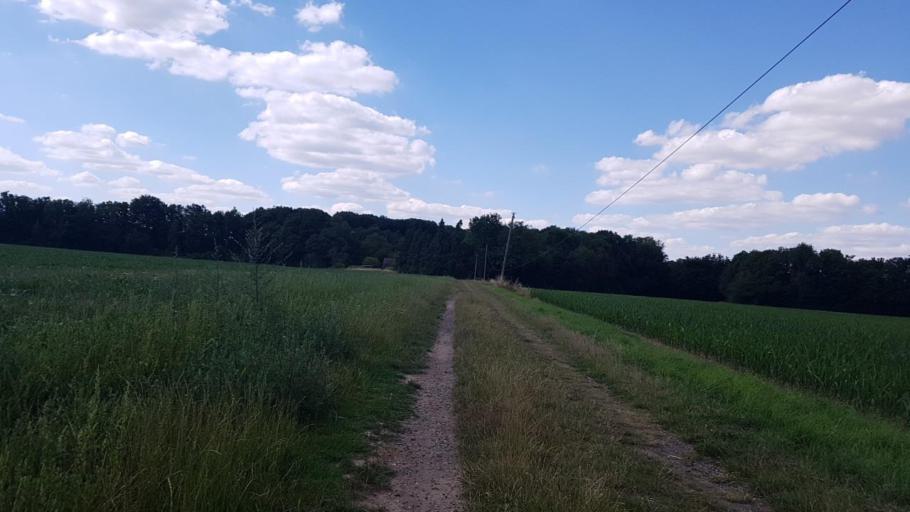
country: FR
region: Picardie
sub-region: Departement de l'Oise
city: Ver-sur-Launette
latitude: 49.1106
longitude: 2.6803
